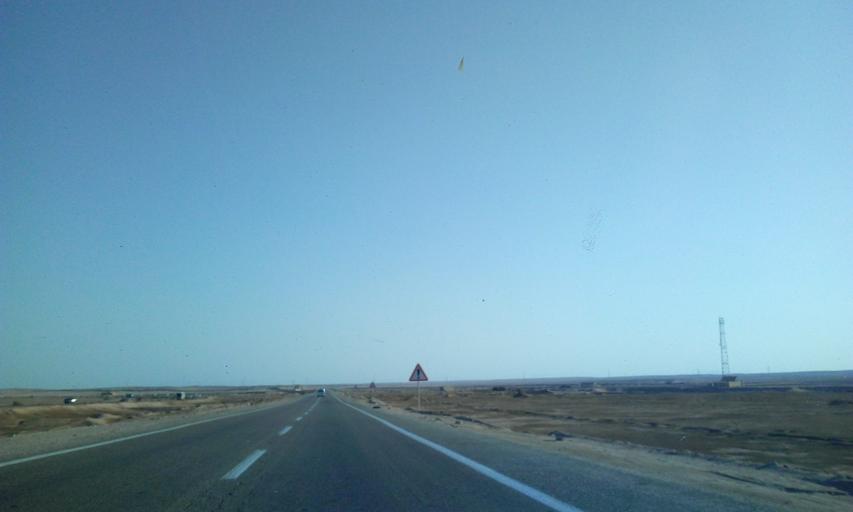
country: EG
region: South Sinai
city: Tor
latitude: 28.5808
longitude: 32.8623
